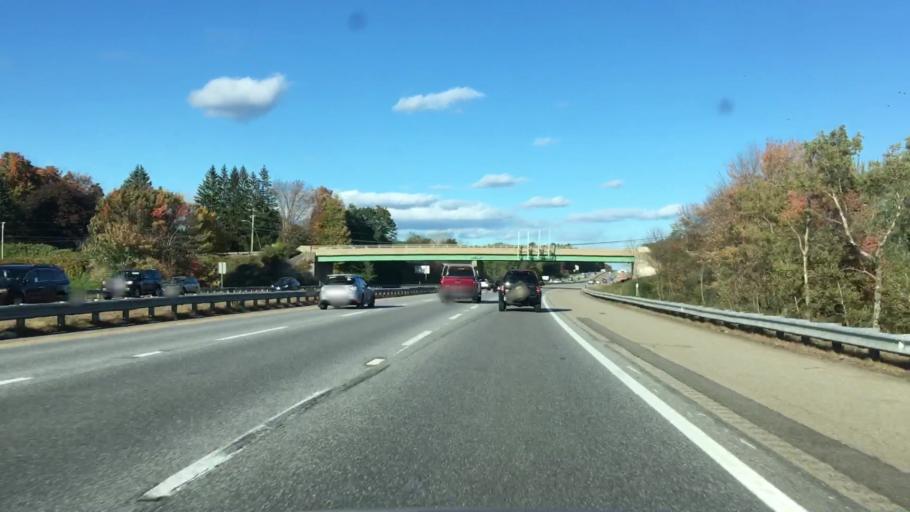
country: US
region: Maine
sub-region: York County
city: Biddeford
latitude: 43.5025
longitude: -70.4853
